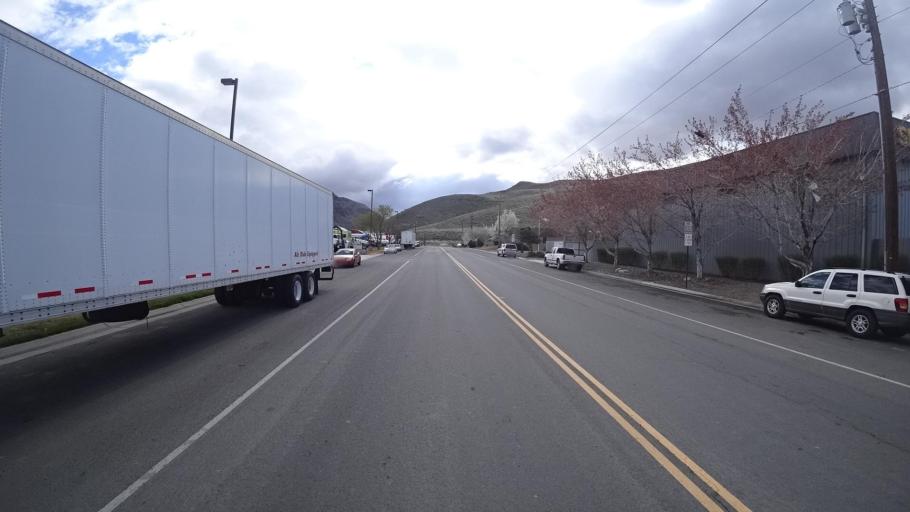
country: US
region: Nevada
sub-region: Washoe County
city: Sparks
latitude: 39.5217
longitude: -119.6986
